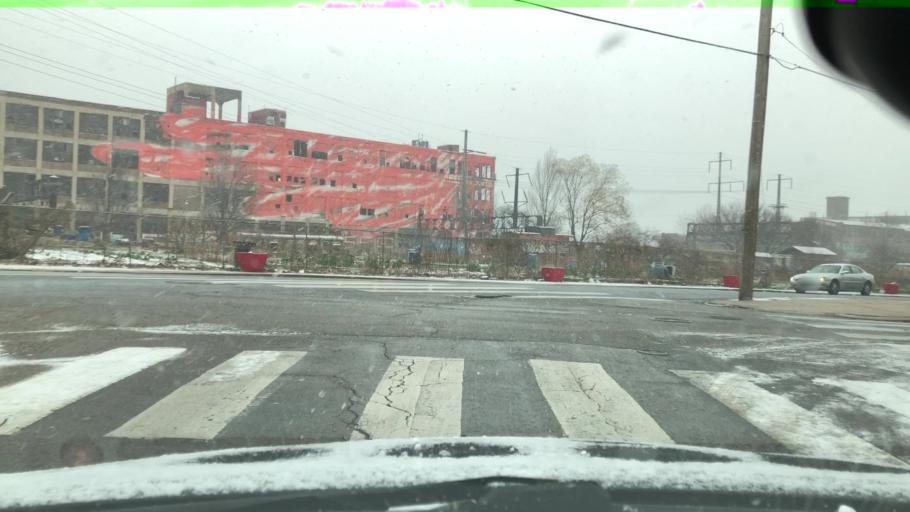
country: US
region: Pennsylvania
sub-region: Philadelphia County
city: Philadelphia
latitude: 39.9933
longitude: -75.1629
